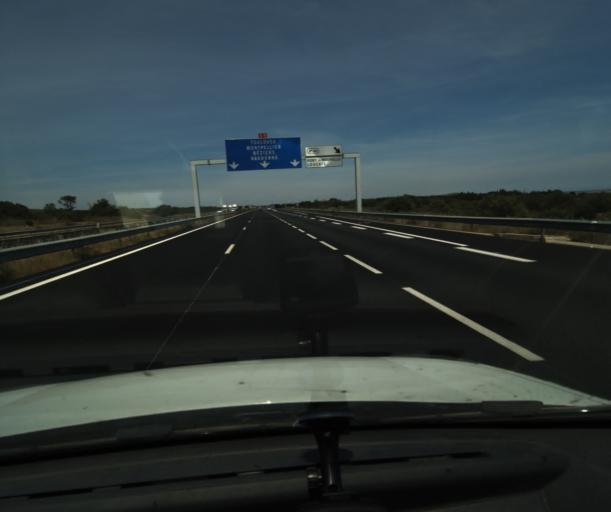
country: FR
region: Languedoc-Roussillon
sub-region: Departement de l'Aude
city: Leucate
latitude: 42.9355
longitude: 2.9696
